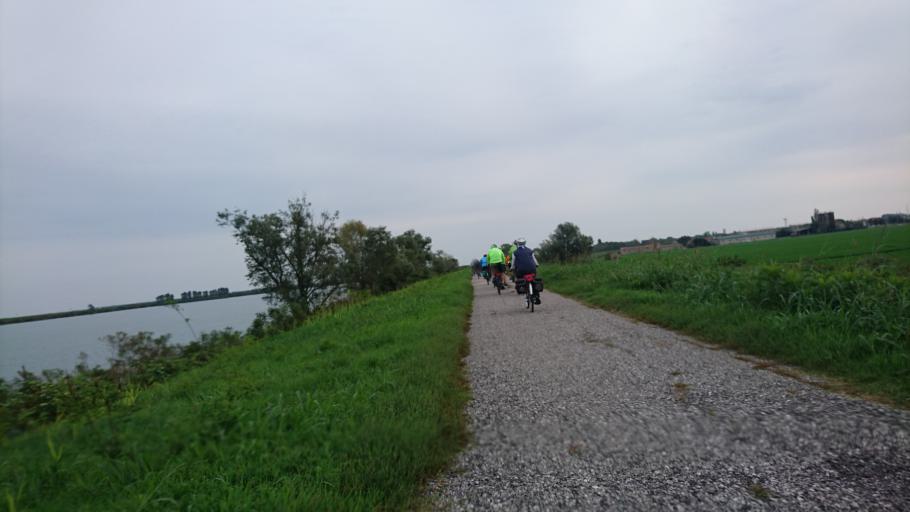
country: IT
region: Veneto
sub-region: Provincia di Rovigo
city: Ca' Tiepolo
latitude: 44.9581
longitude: 12.4007
